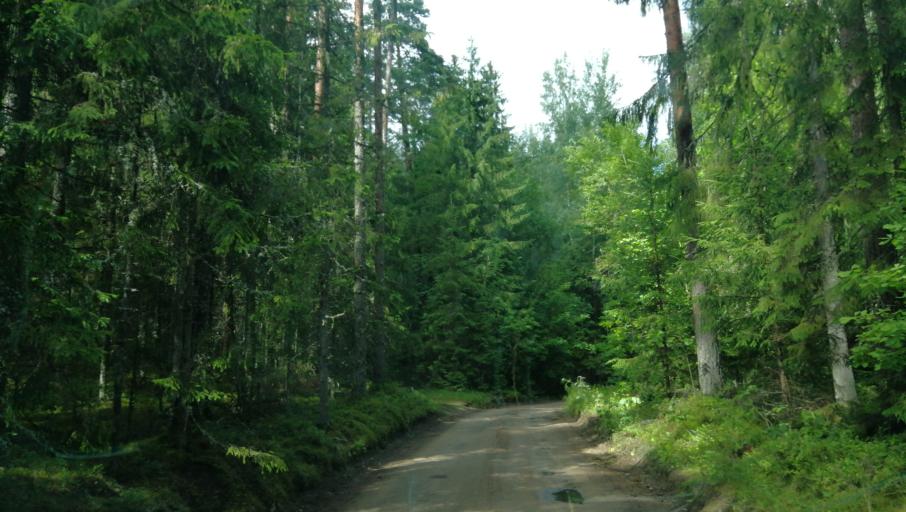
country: LV
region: Cesu Rajons
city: Cesis
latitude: 57.3022
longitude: 25.2096
